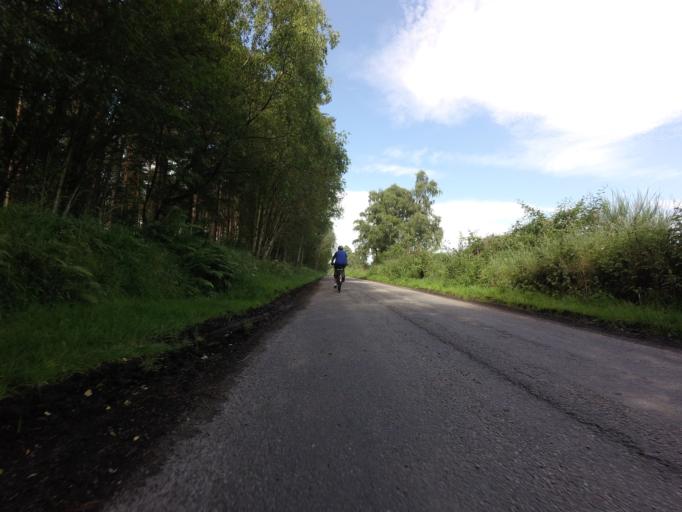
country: GB
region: Scotland
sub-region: Highland
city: Inverness
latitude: 57.5184
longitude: -4.2917
